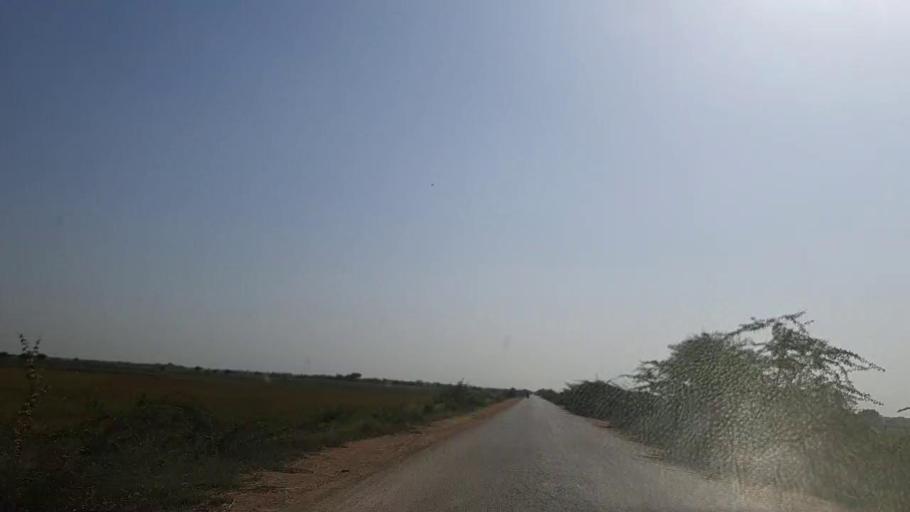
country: PK
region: Sindh
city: Mirpur Batoro
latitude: 24.5910
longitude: 68.2920
